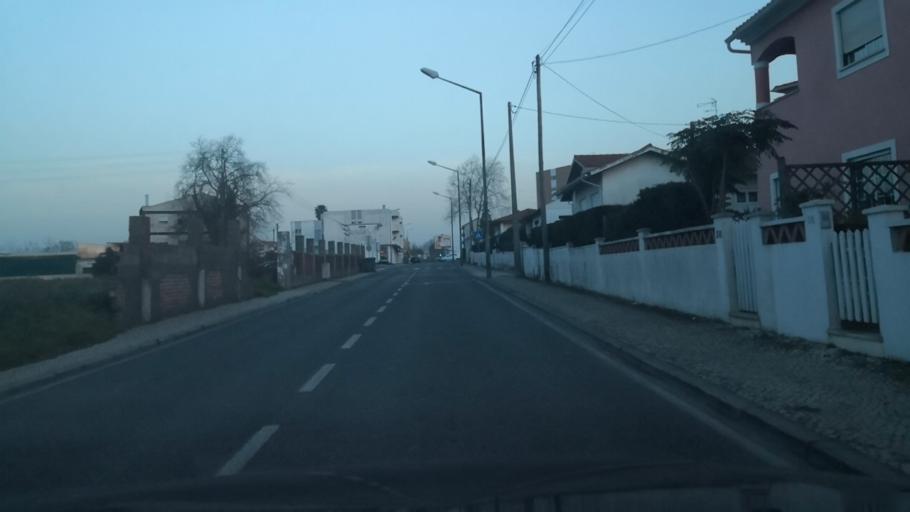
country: PT
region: Leiria
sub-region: Marinha Grande
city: Marinha Grande
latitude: 39.7500
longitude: -8.9236
